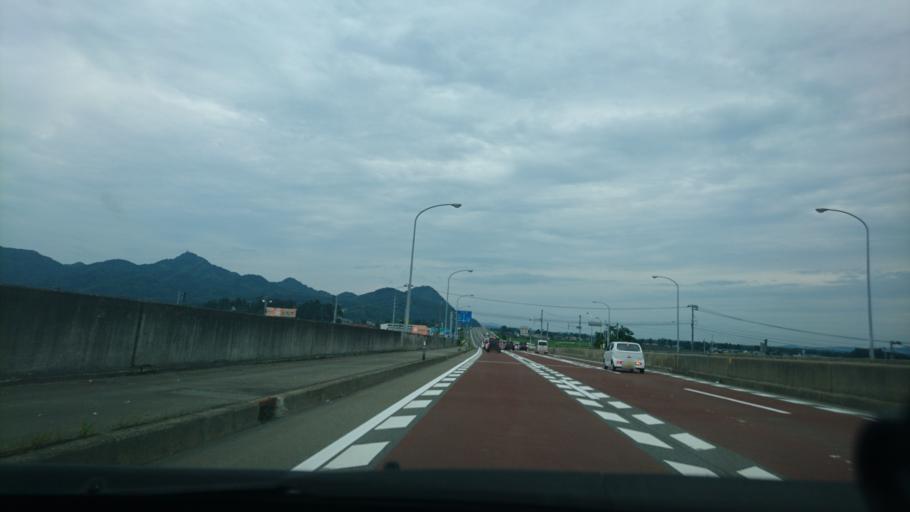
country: JP
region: Akita
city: Omagari
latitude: 39.4745
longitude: 140.4778
